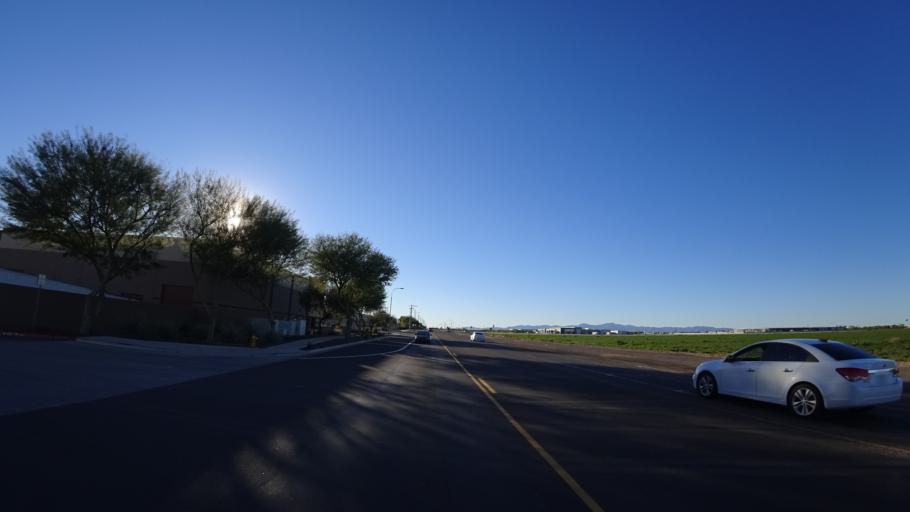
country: US
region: Arizona
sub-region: Maricopa County
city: Tolleson
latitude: 33.4501
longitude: -112.2792
